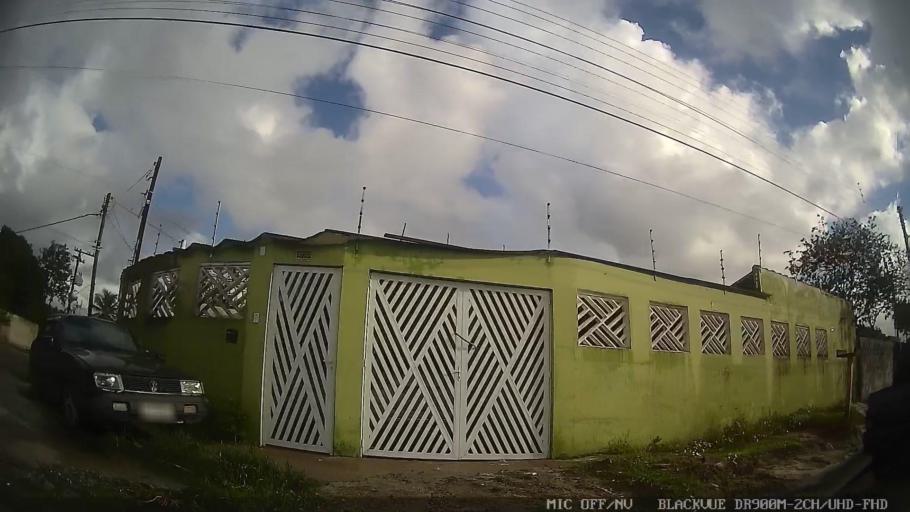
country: BR
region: Sao Paulo
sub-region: Itanhaem
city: Itanhaem
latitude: -24.1771
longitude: -46.8518
